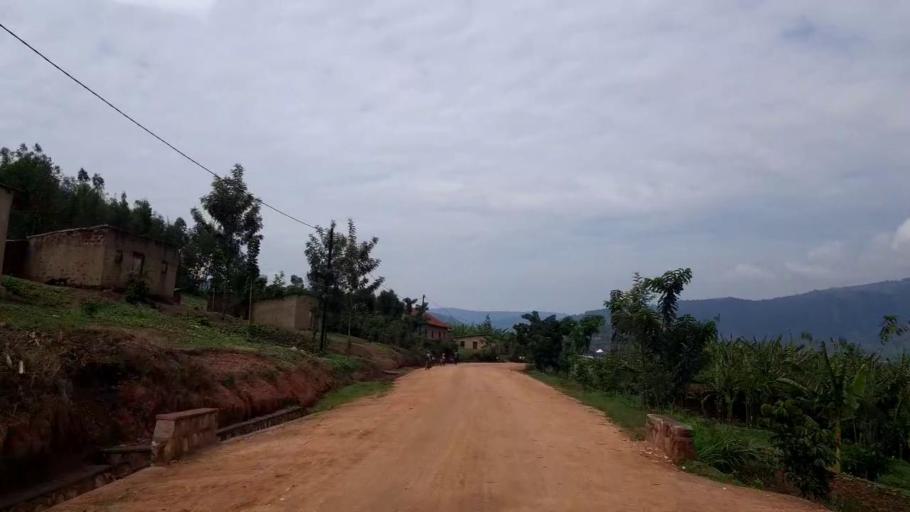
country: RW
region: Northern Province
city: Byumba
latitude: -1.4975
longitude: 30.2236
